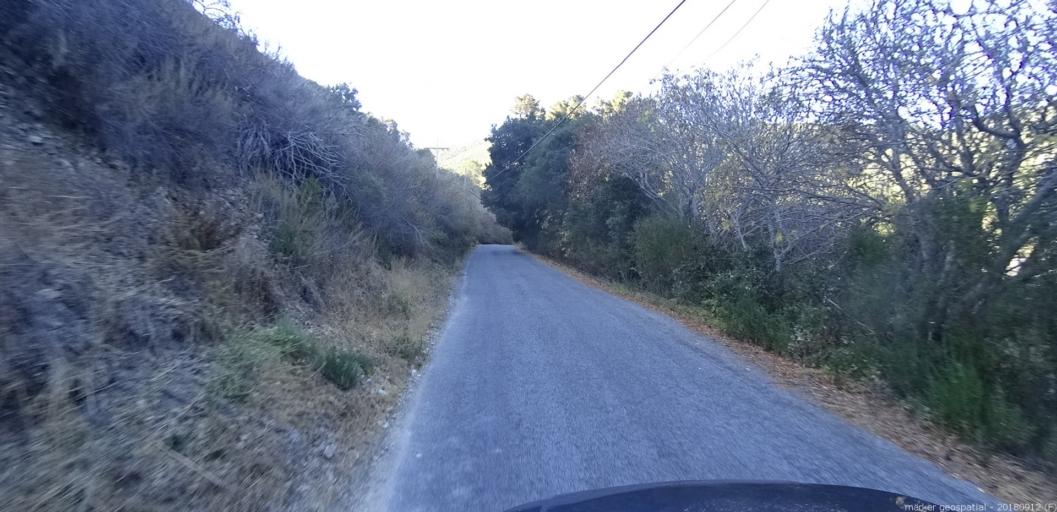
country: US
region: California
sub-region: Monterey County
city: Carmel Valley Village
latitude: 36.5367
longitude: -121.7378
